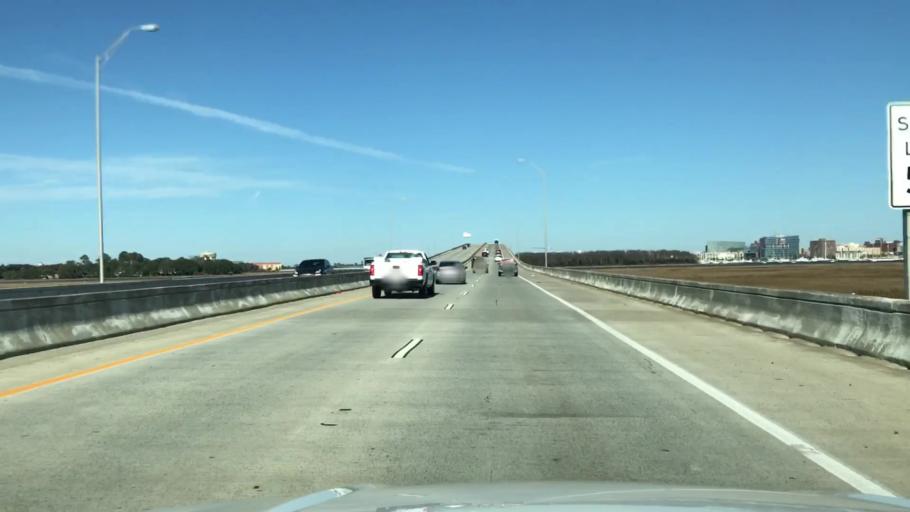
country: US
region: South Carolina
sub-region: Charleston County
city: Charleston
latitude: 32.7635
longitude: -79.9580
